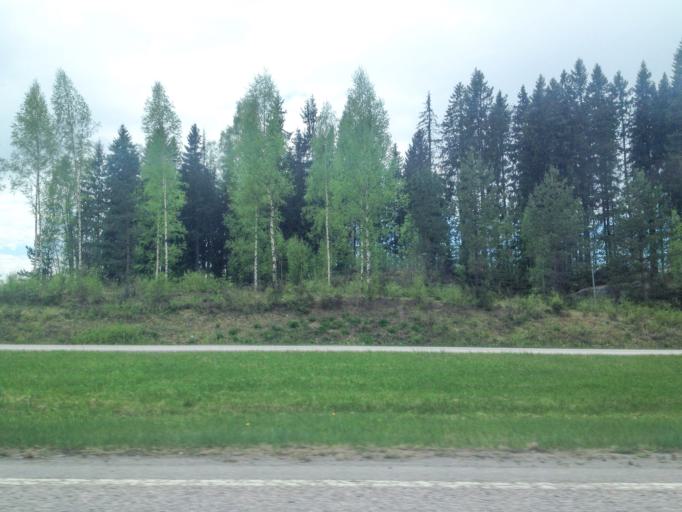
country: FI
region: Uusimaa
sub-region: Helsinki
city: Hyvinge
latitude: 60.5681
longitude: 24.8177
